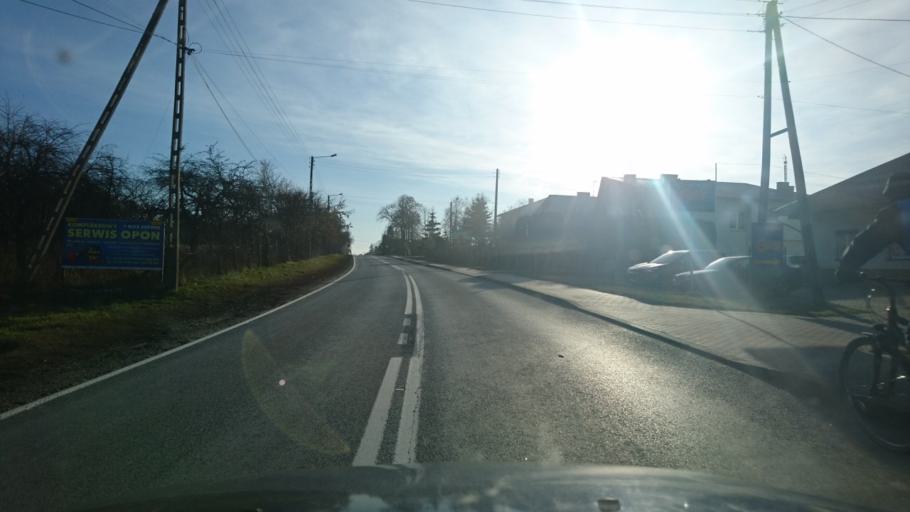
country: PL
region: Opole Voivodeship
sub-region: Powiat oleski
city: Dalachow
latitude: 51.0436
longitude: 18.5967
